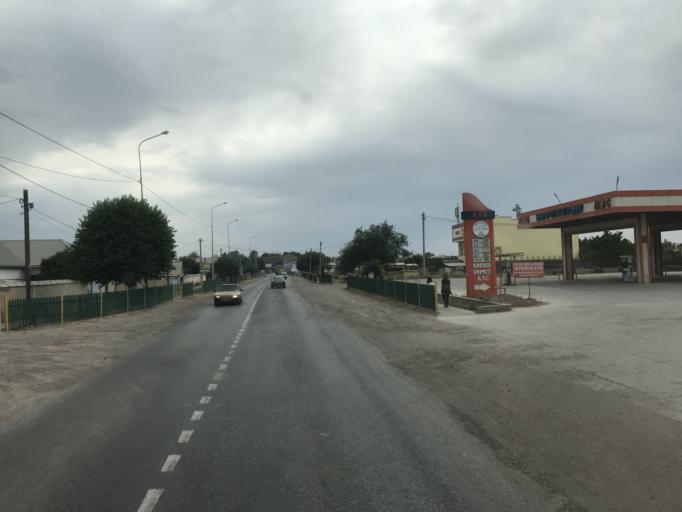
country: KZ
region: Ongtustik Qazaqstan
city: Saryaghash
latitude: 41.3457
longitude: 68.9577
